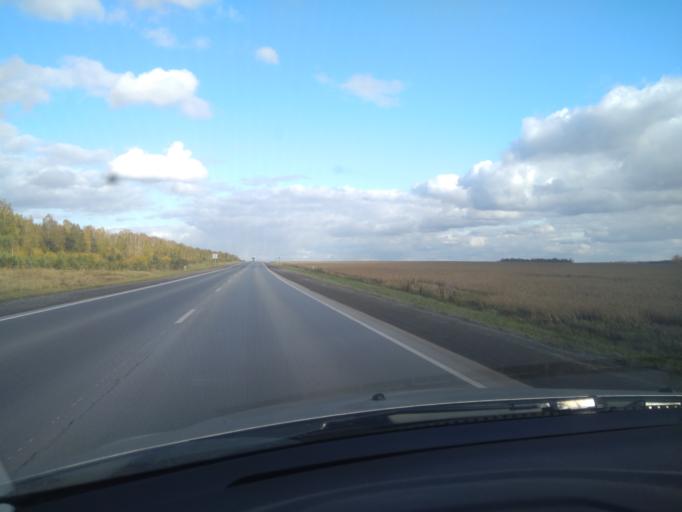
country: RU
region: Sverdlovsk
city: Tugulym
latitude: 57.0678
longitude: 64.6632
